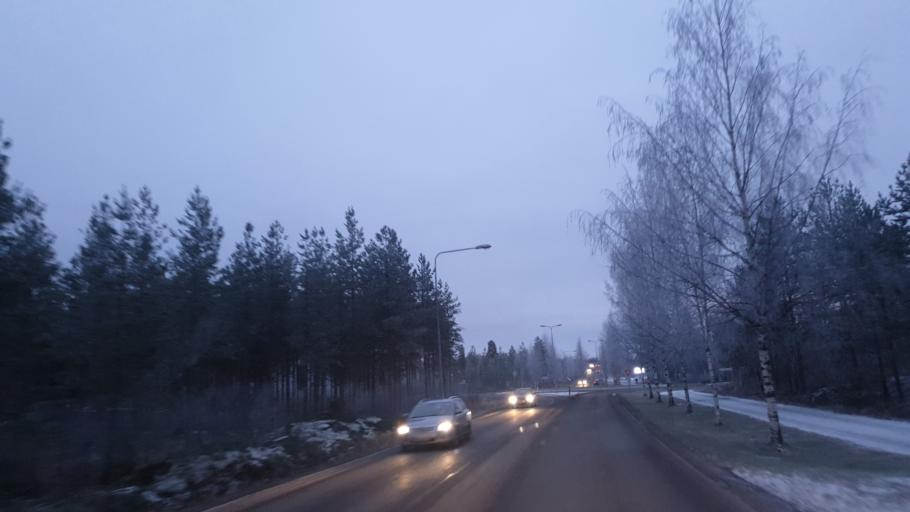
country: FI
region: Southern Ostrobothnia
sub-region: Seinaejoki
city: Nurmo
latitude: 62.7786
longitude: 22.8955
